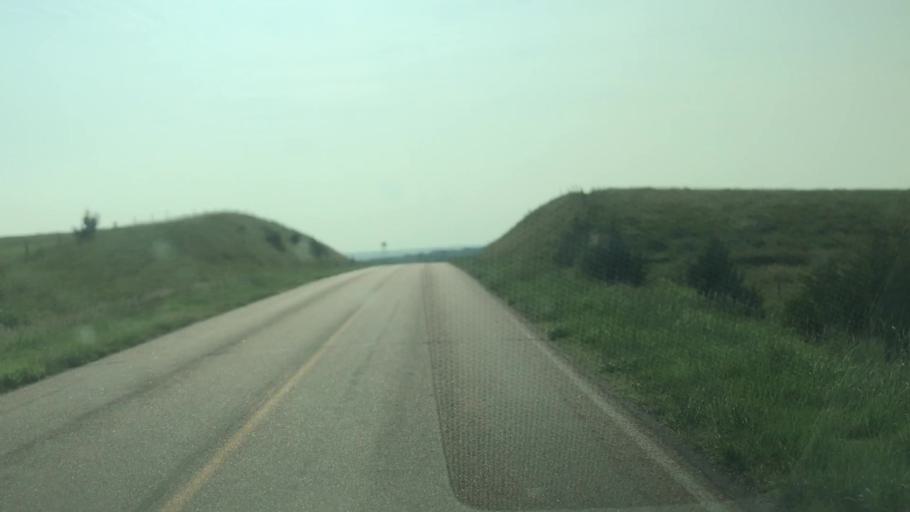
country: US
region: Nebraska
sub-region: Sherman County
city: Loup City
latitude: 41.2793
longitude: -98.9421
